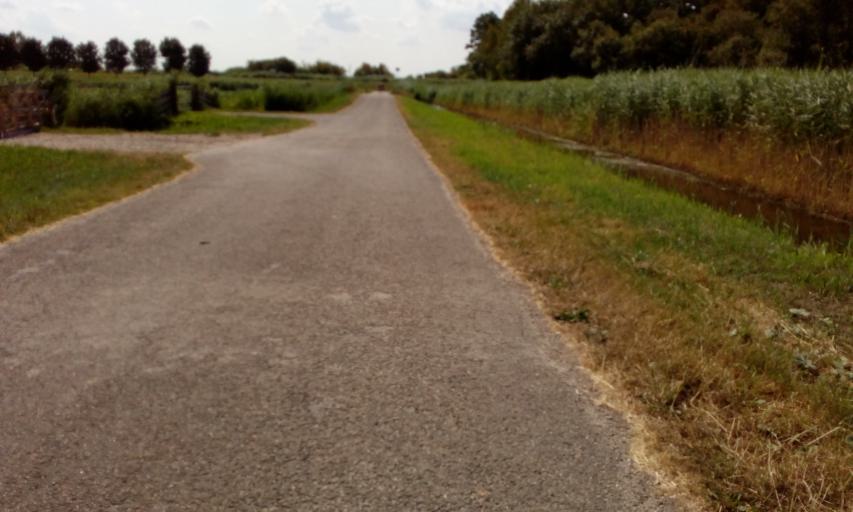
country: NL
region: South Holland
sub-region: Gemeente Maassluis
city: Maassluis
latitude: 51.9345
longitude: 4.2845
